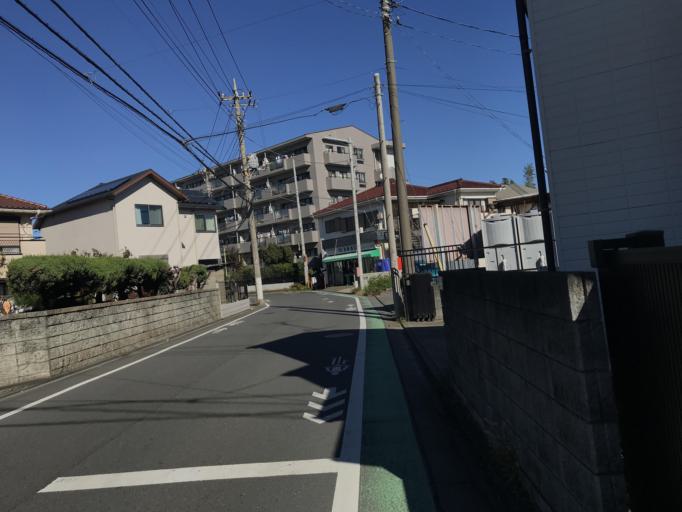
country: JP
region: Tokyo
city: Tanashicho
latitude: 35.7538
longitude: 139.5127
